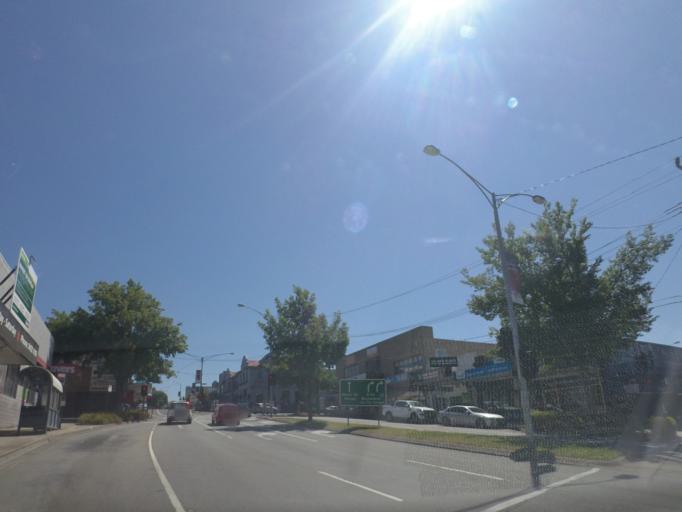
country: AU
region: Victoria
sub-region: Banyule
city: Greensborough
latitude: -37.7027
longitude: 145.1058
